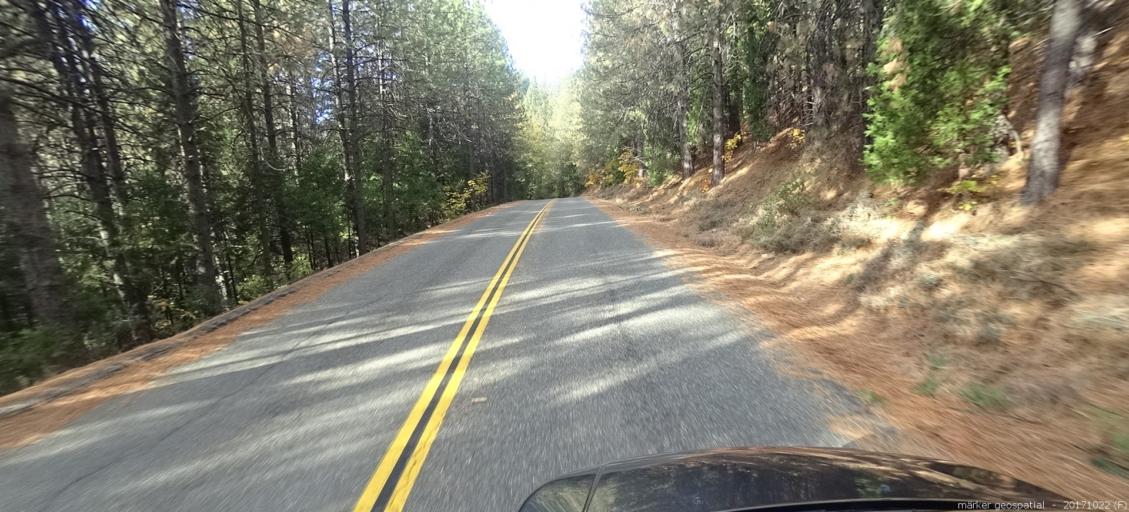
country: US
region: California
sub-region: Siskiyou County
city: Dunsmuir
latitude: 41.1525
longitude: -122.2974
